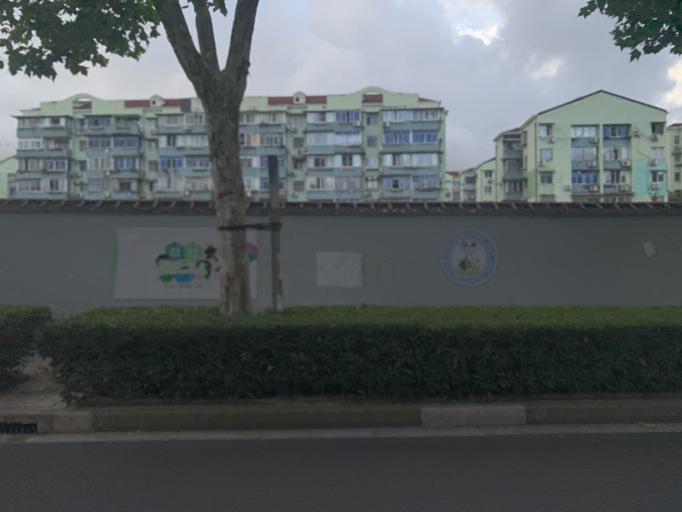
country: CN
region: Shanghai Shi
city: Pudong
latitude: 31.2507
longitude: 121.5751
